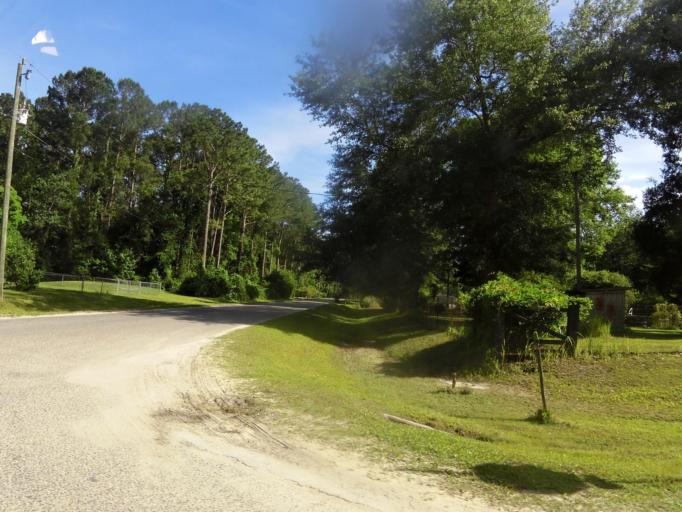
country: US
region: Florida
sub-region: Nassau County
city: Callahan
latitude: 30.5626
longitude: -81.8000
